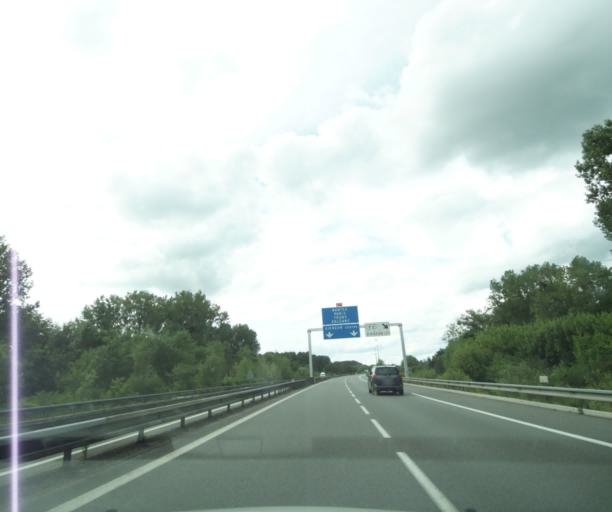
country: FR
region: Centre
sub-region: Departement du Cher
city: Vierzon
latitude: 47.2050
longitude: 2.1247
